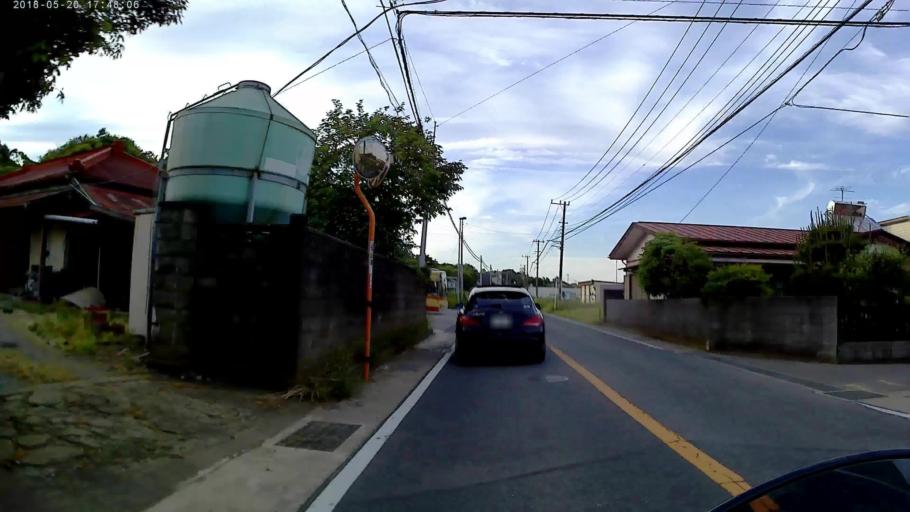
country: JP
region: Kanagawa
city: Oiso
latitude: 35.3379
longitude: 139.2929
